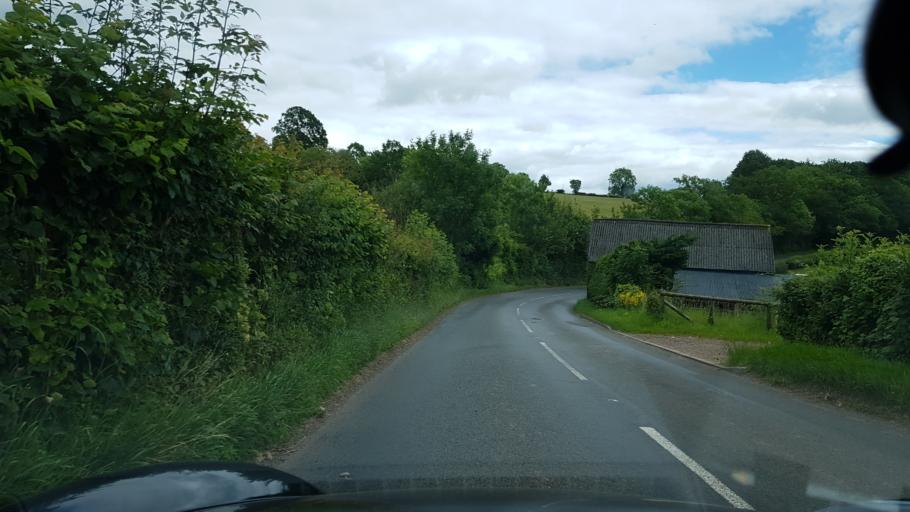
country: GB
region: Wales
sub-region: Monmouthshire
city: Grosmont
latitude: 51.8733
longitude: -2.8544
